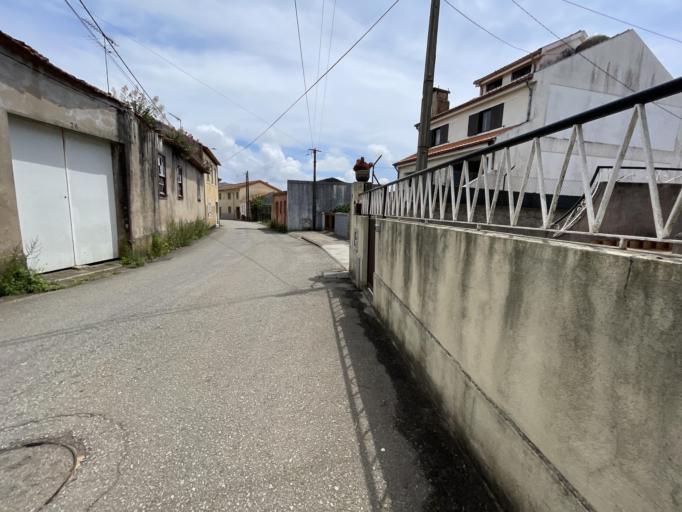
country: PT
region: Aveiro
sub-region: Ovar
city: Cortegaca
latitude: 40.9468
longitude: -8.6247
